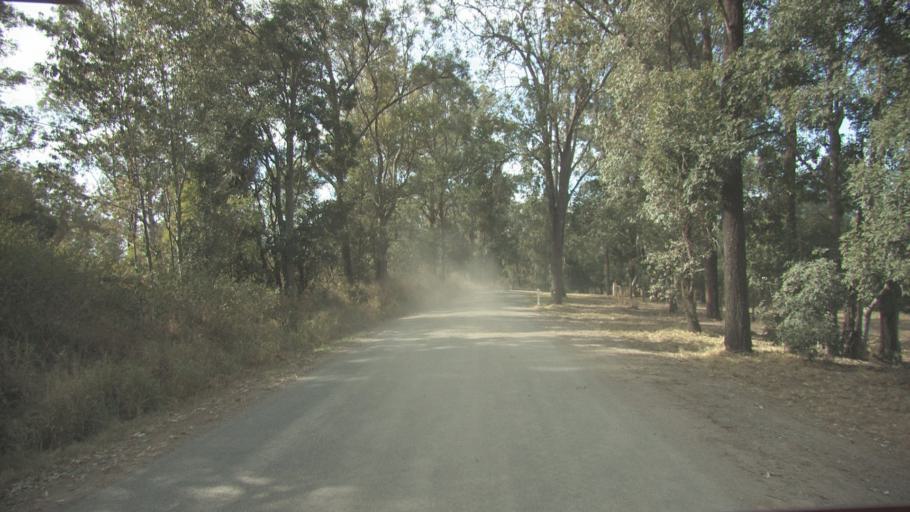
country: AU
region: Queensland
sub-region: Logan
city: Cedar Vale
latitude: -27.8964
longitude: 152.9892
